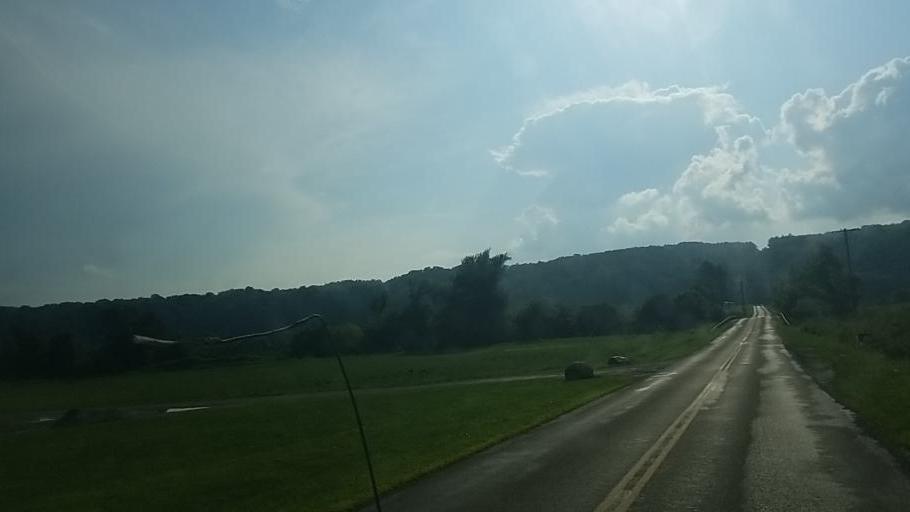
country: US
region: Ohio
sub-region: Wayne County
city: Wooster
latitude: 40.8580
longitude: -82.0048
